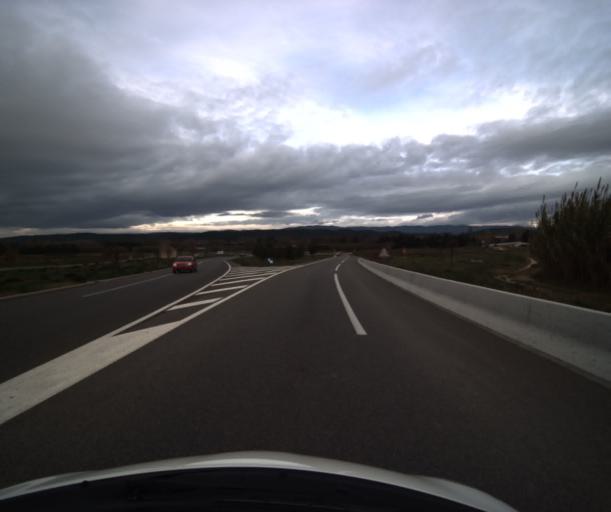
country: FR
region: Provence-Alpes-Cote d'Azur
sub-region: Departement du Vaucluse
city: Pertuis
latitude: 43.6860
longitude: 5.4836
